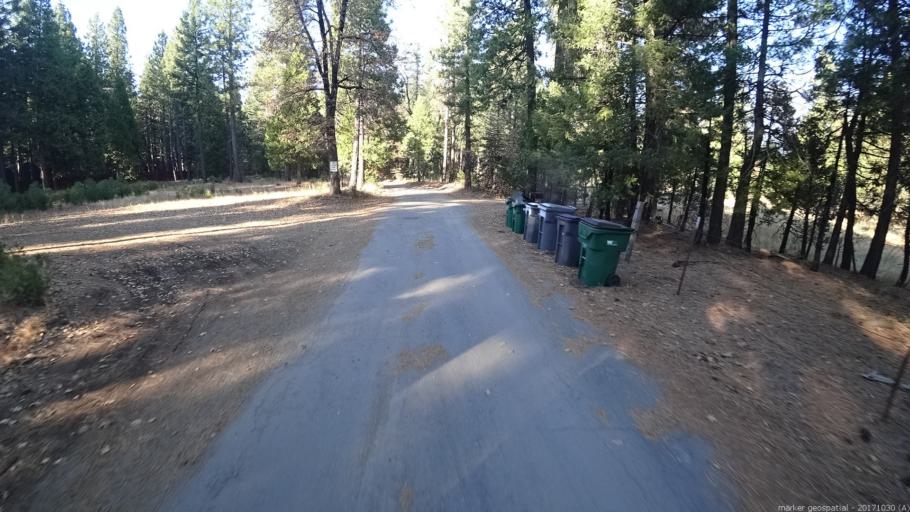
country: US
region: California
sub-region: Shasta County
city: Shingletown
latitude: 40.5649
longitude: -121.7205
